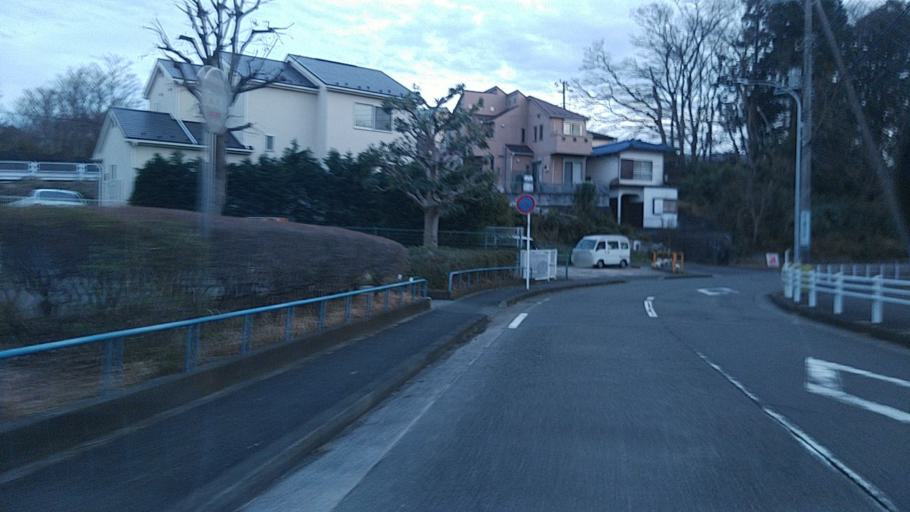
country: JP
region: Kanagawa
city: Fujisawa
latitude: 35.4125
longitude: 139.4921
